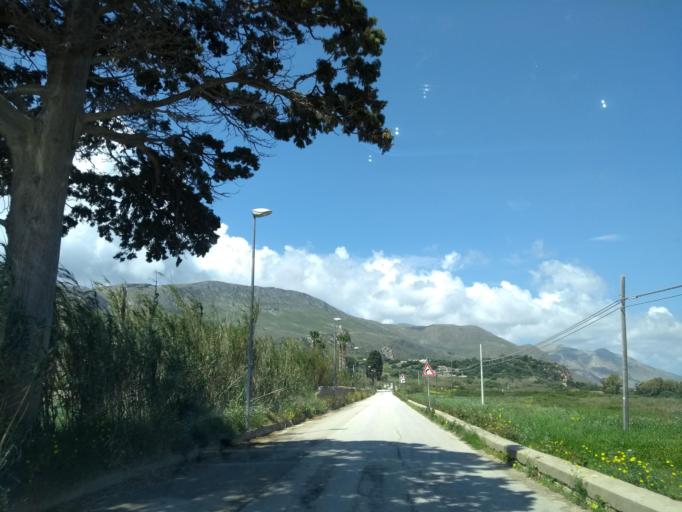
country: IT
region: Sicily
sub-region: Trapani
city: Castellammare del Golfo
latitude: 38.0626
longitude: 12.8263
